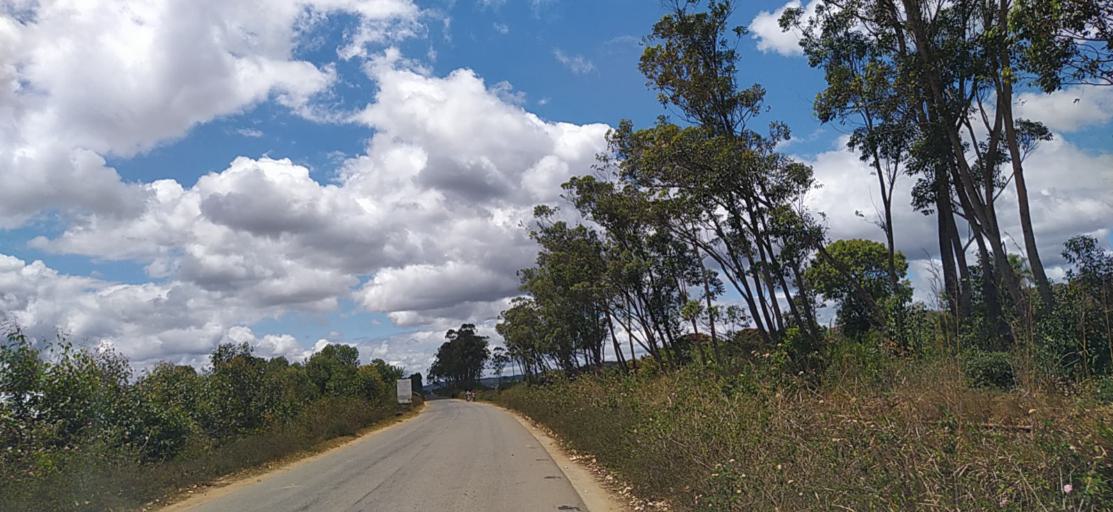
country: MG
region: Alaotra Mangoro
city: Moramanga
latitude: -18.7794
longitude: 48.2486
